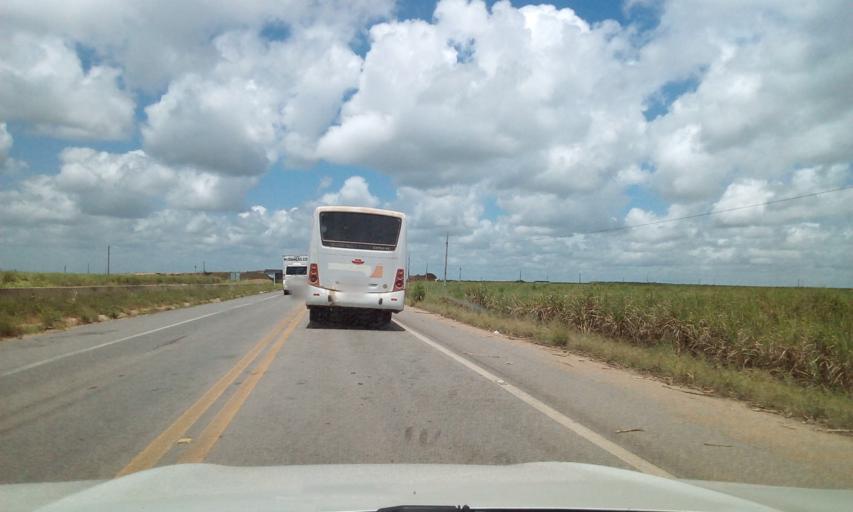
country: BR
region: Alagoas
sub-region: Sao Miguel Dos Campos
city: Sao Miguel dos Campos
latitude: -9.7596
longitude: -36.0706
